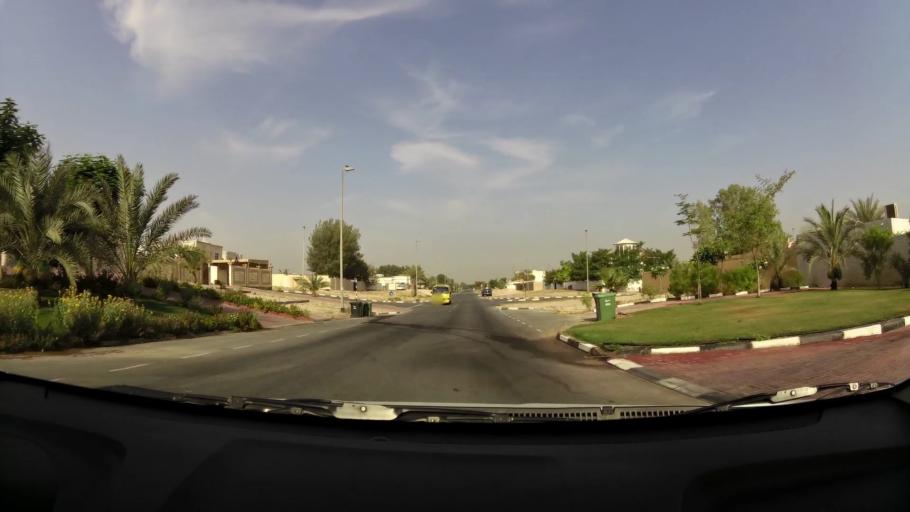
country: AE
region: Ash Shariqah
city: Sharjah
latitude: 25.2459
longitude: 55.4124
